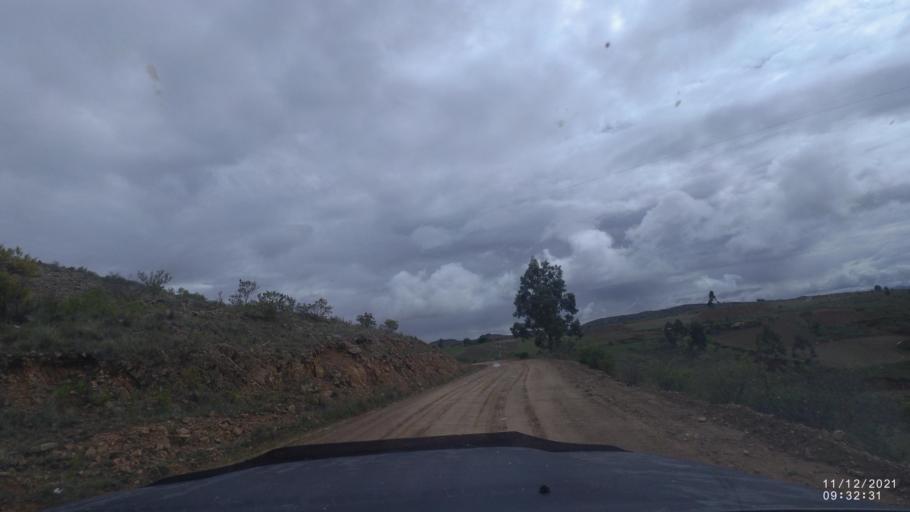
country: BO
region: Cochabamba
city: Tarata
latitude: -17.8435
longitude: -65.9898
